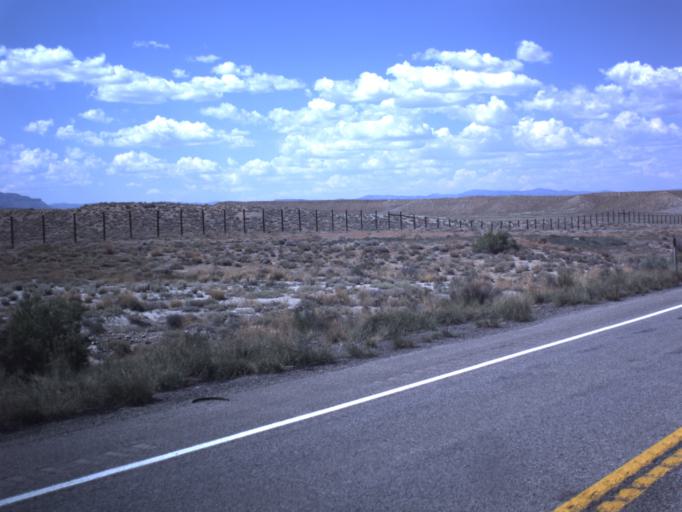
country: US
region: Utah
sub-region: Emery County
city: Huntington
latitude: 39.4290
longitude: -110.8688
